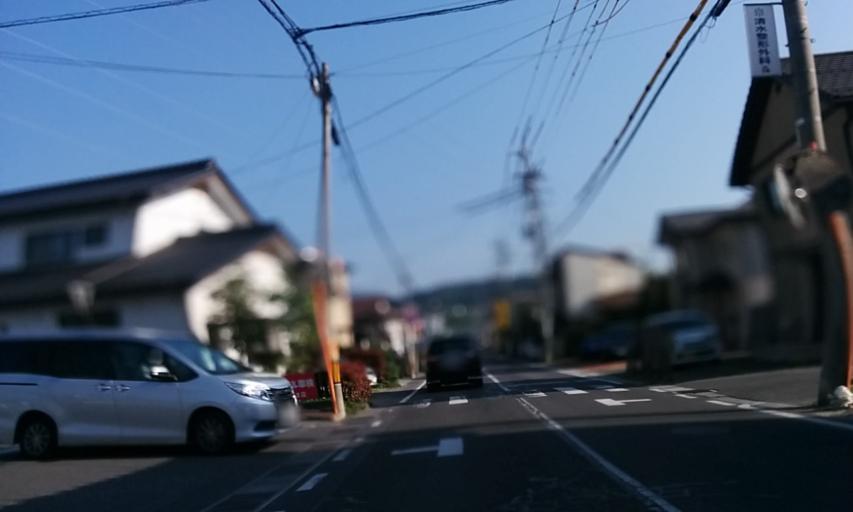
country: JP
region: Nagano
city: Matsumoto
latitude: 36.2237
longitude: 137.9857
